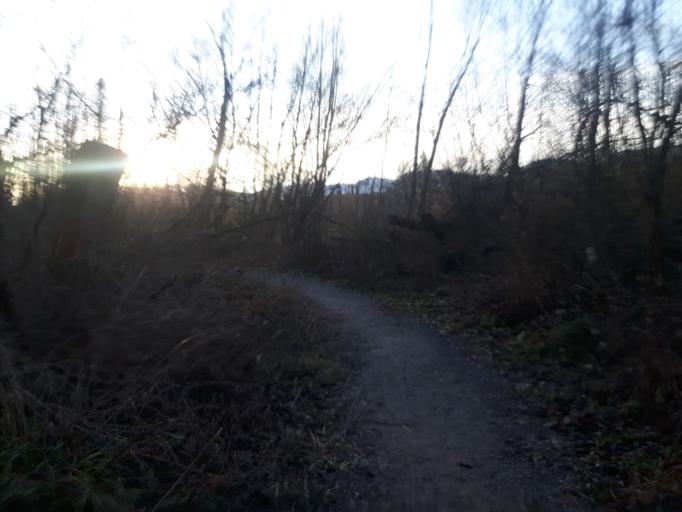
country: DE
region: Baden-Wuerttemberg
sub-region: Regierungsbezirk Stuttgart
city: Heilbronn
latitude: 49.1345
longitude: 9.2531
